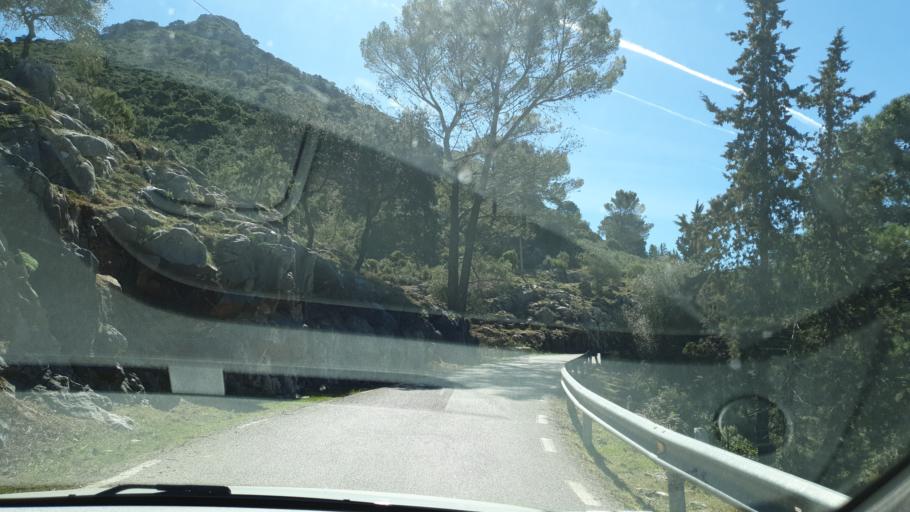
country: ES
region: Andalusia
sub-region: Provincia de Malaga
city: Ojen
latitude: 36.5823
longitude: -4.8841
